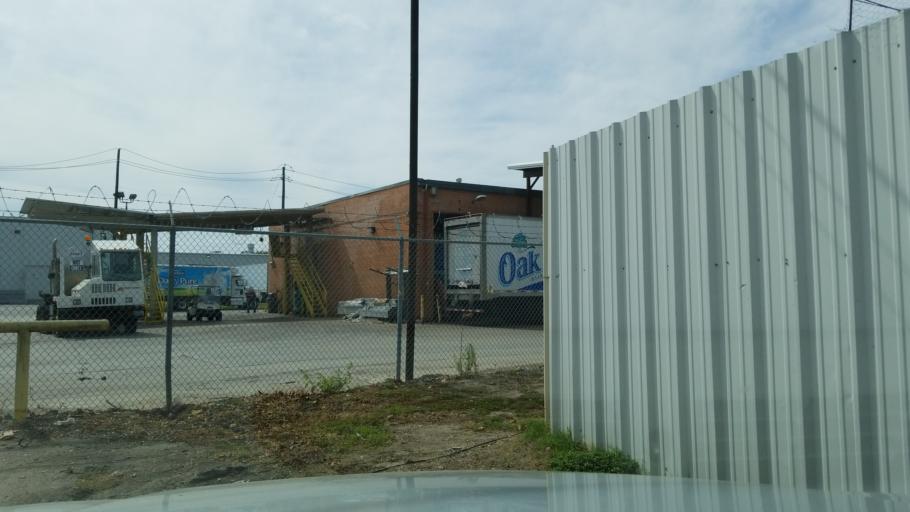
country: US
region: Texas
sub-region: Dallas County
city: Dallas
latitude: 32.7851
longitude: -96.7389
